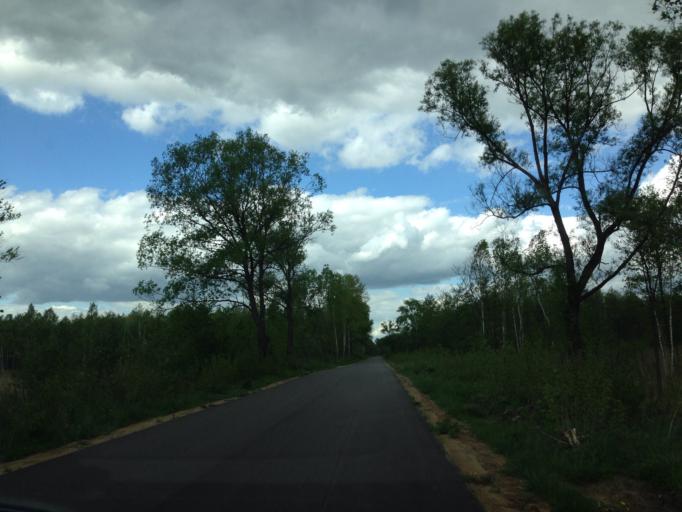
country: PL
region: Podlasie
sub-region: Powiat bialostocki
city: Tykocin
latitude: 53.3062
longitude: 22.6039
